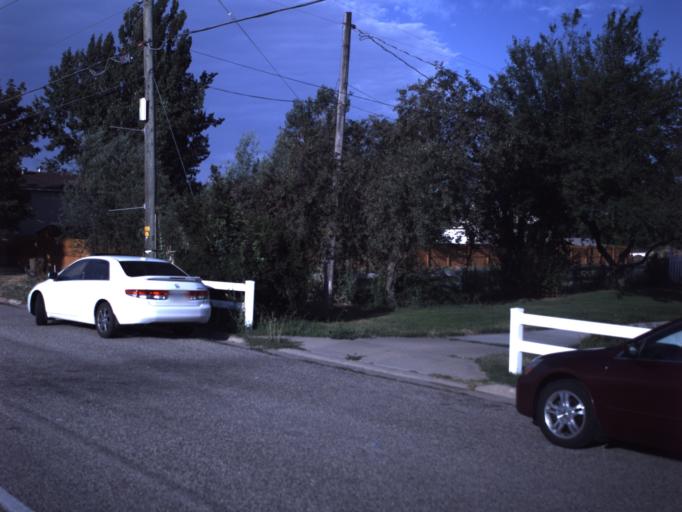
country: US
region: Utah
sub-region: Weber County
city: Plain City
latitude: 41.2927
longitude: -112.0930
